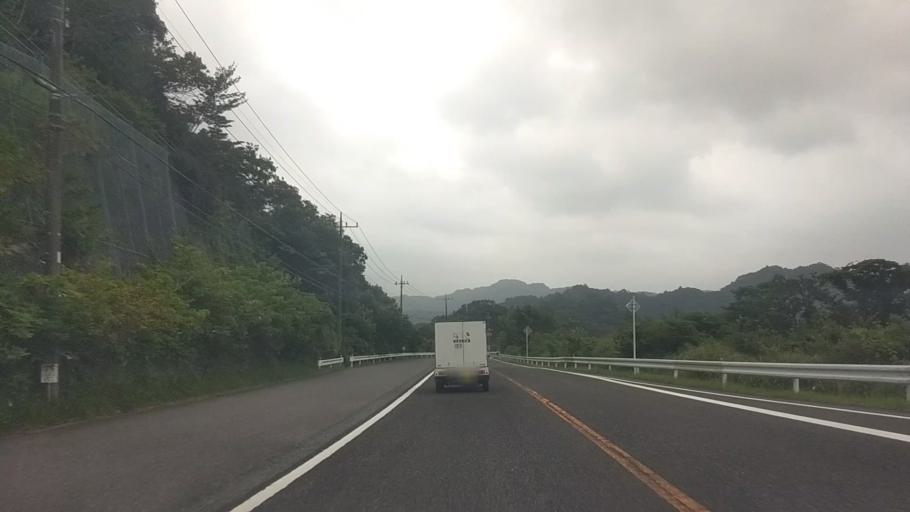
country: JP
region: Chiba
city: Kawaguchi
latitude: 35.1616
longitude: 140.0627
